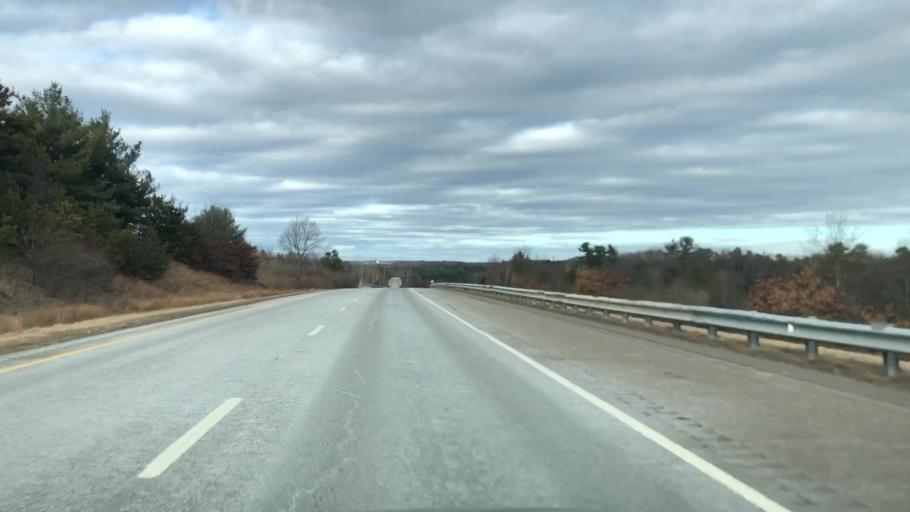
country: US
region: Massachusetts
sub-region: Worcester County
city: Leominster
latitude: 42.4880
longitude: -71.7234
